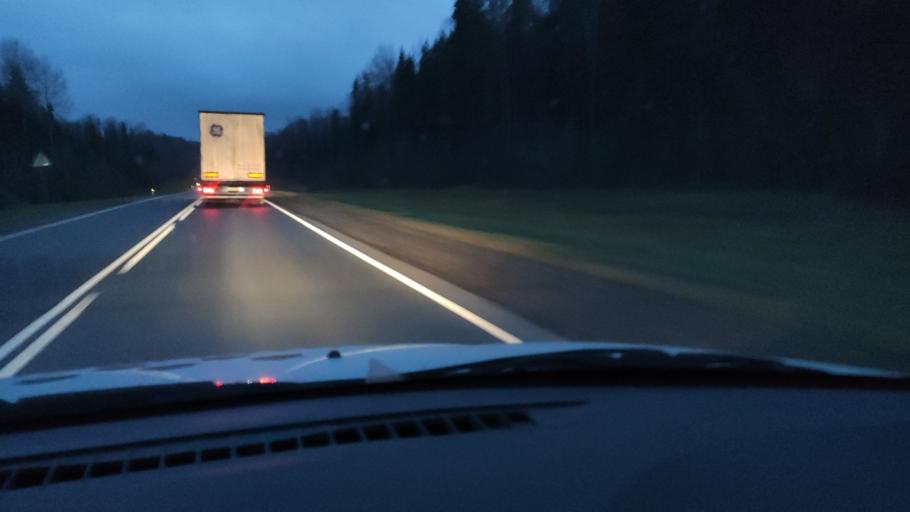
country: RU
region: Kirov
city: Kostino
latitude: 58.8273
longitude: 53.5367
